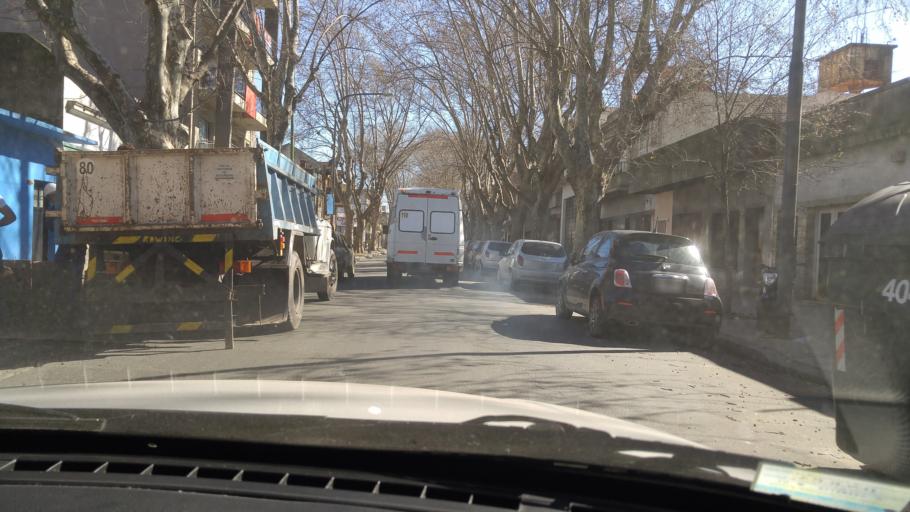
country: AR
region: Buenos Aires F.D.
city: Villa Santa Rita
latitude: -34.6248
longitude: -58.4882
